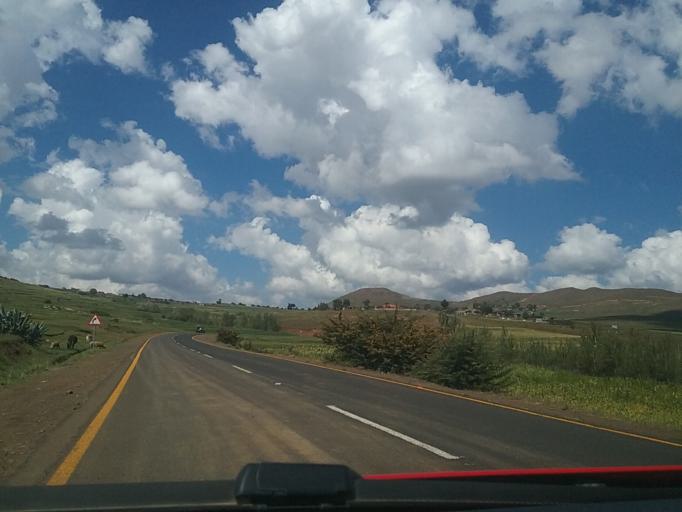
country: LS
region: Berea
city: Teyateyaneng
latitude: -29.2200
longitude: 27.8556
